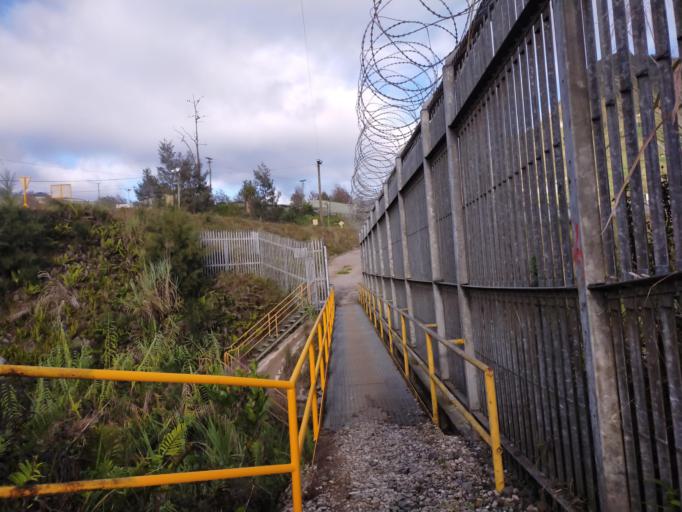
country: PG
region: Enga
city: Porgera
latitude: -5.4644
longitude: 143.1049
